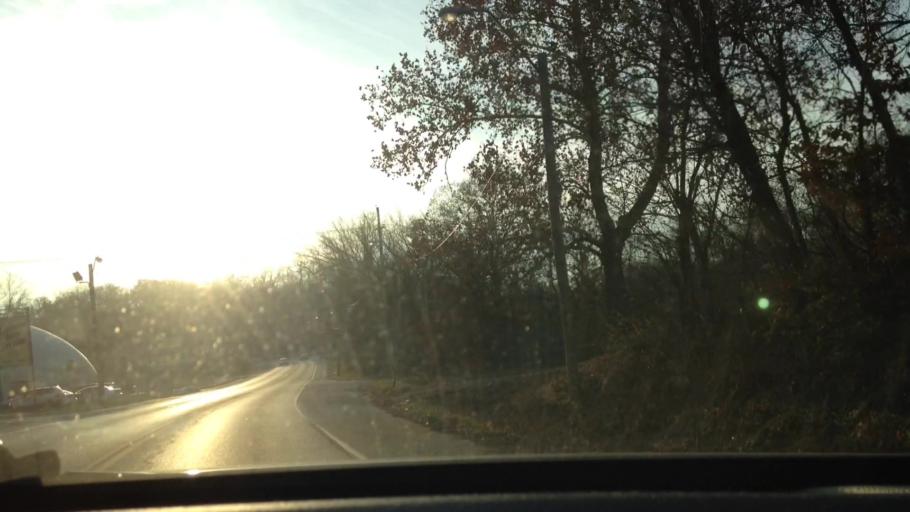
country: US
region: Missouri
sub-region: Clay County
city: Gladstone
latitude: 39.1687
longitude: -94.5506
